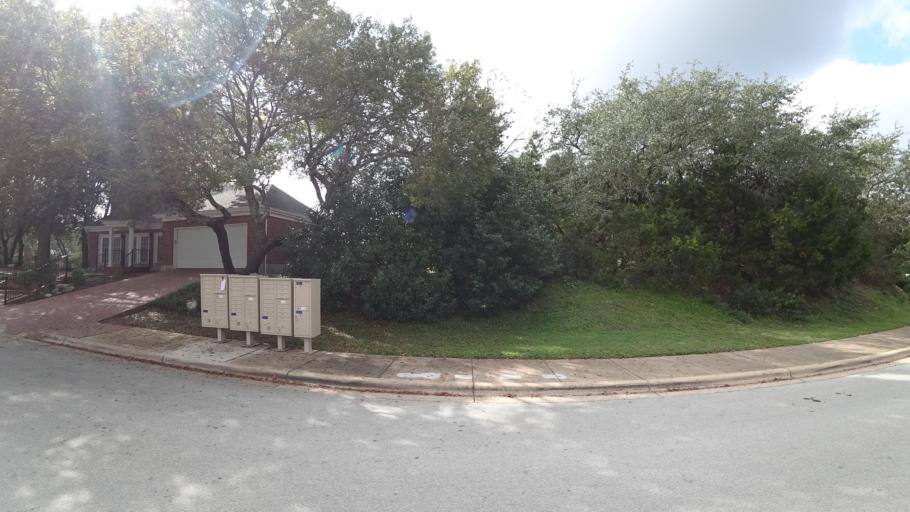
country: US
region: Texas
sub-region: Travis County
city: Barton Creek
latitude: 30.3022
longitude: -97.8925
